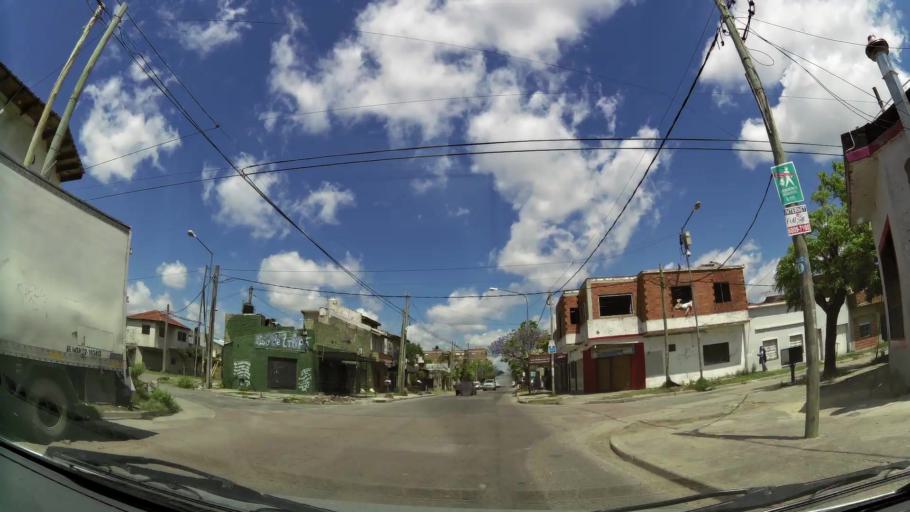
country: AR
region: Buenos Aires
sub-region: Partido de Lanus
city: Lanus
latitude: -34.6961
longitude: -58.4242
